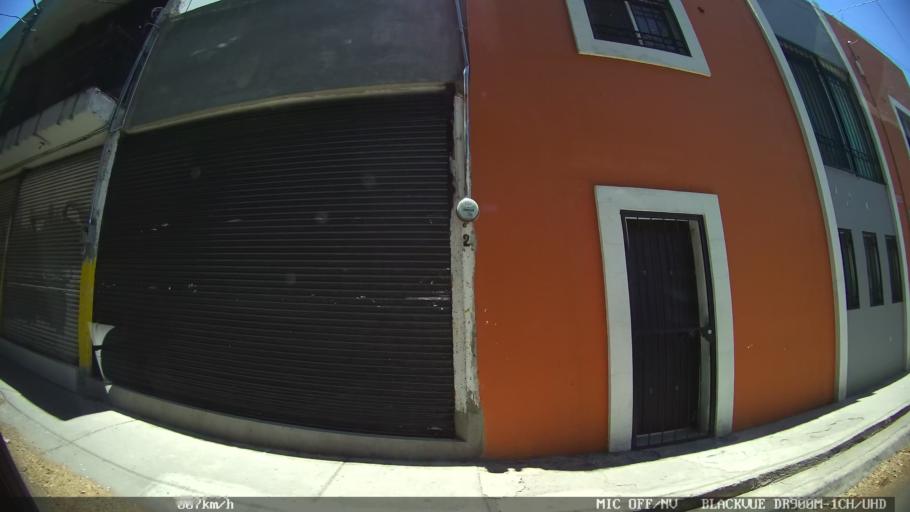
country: MX
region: Jalisco
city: Tlaquepaque
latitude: 20.6664
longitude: -103.2961
